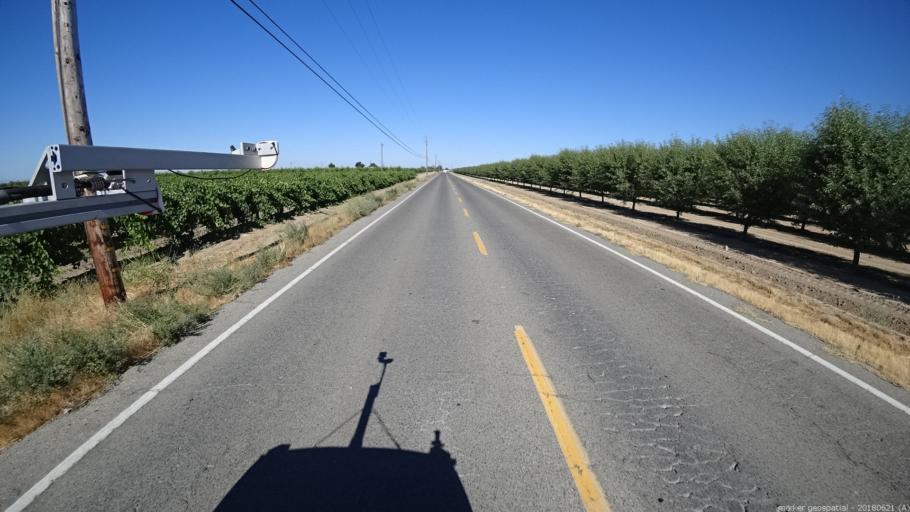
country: US
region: California
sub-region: Fresno County
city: Biola
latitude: 36.8513
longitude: -120.0410
